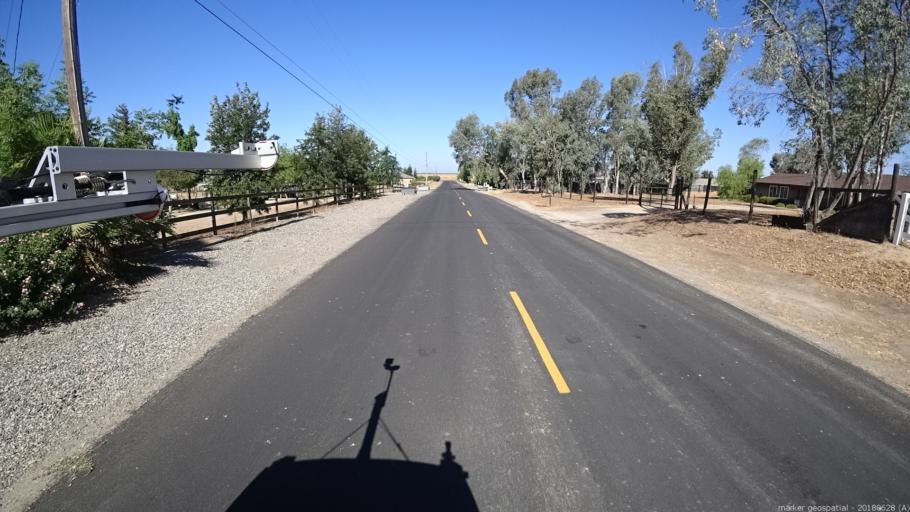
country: US
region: California
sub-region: Madera County
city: Bonadelle Ranchos-Madera Ranchos
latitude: 37.0085
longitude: -119.8908
